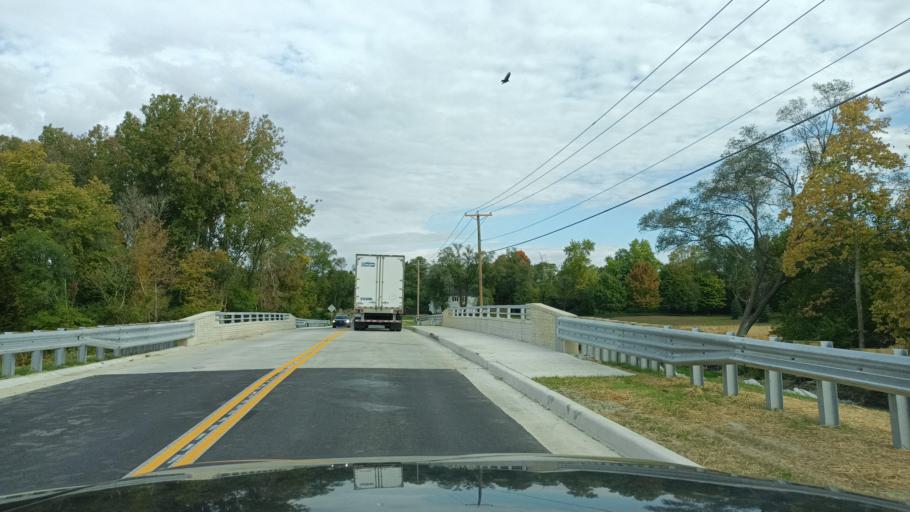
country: US
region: Indiana
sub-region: Delaware County
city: Yorktown
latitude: 40.1939
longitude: -85.4617
